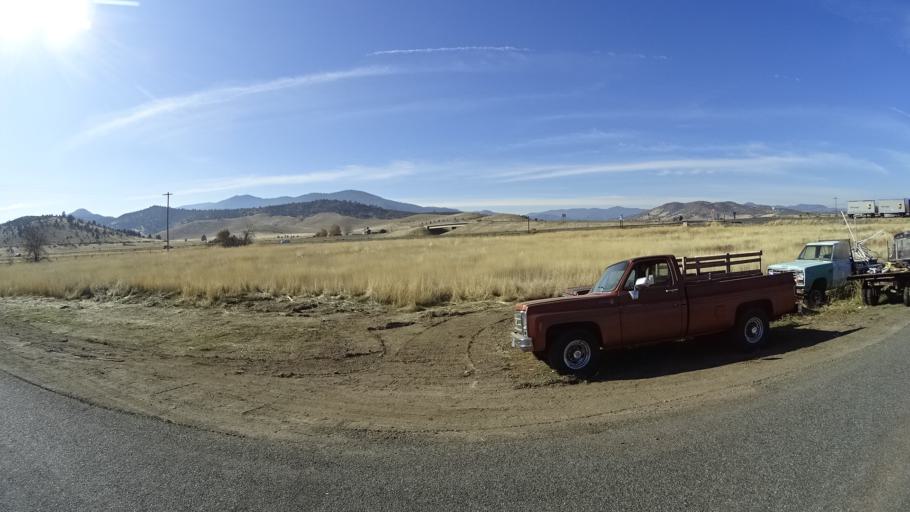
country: US
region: California
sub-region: Siskiyou County
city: Montague
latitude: 41.6460
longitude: -122.5320
